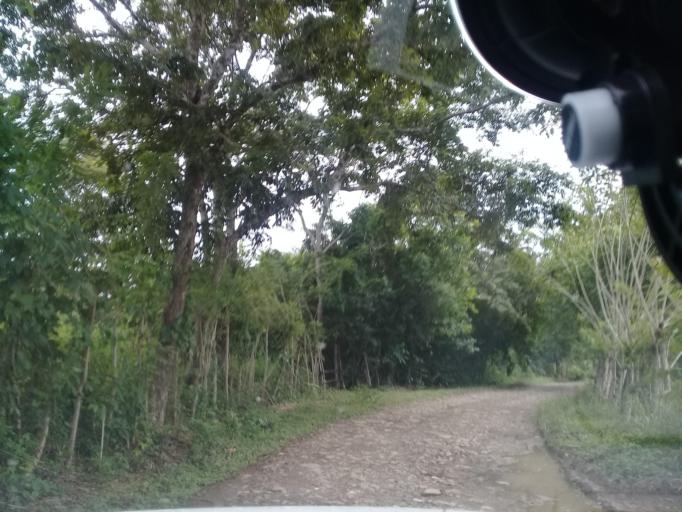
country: MX
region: Hidalgo
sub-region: Huejutla de Reyes
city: Parque de Poblamiento Solidaridad
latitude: 21.1771
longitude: -98.3773
